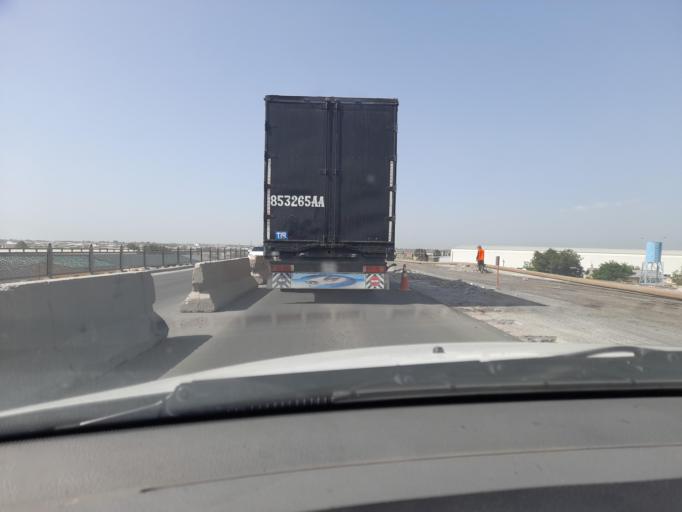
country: UZ
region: Samarqand
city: Samarqand
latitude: 39.6972
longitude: 67.0194
